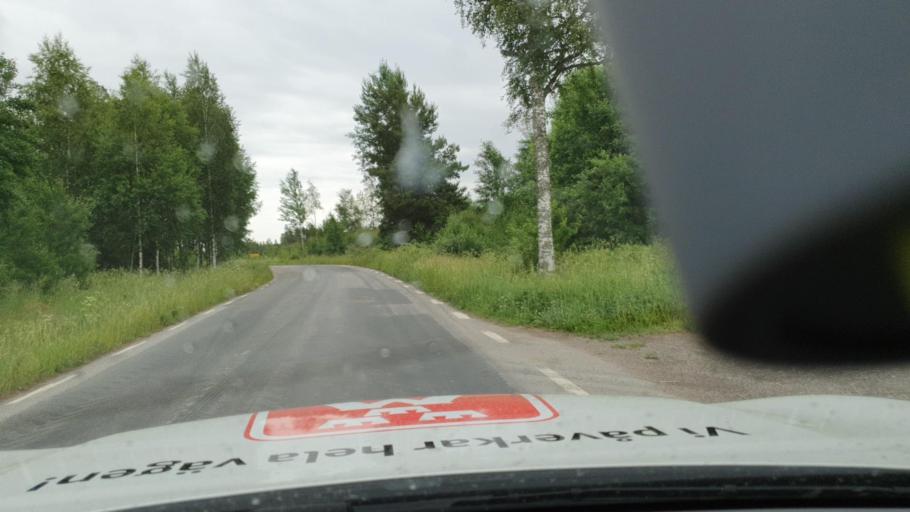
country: SE
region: Vaestra Goetaland
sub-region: Tidaholms Kommun
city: Olofstorp
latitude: 58.3421
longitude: 14.0075
